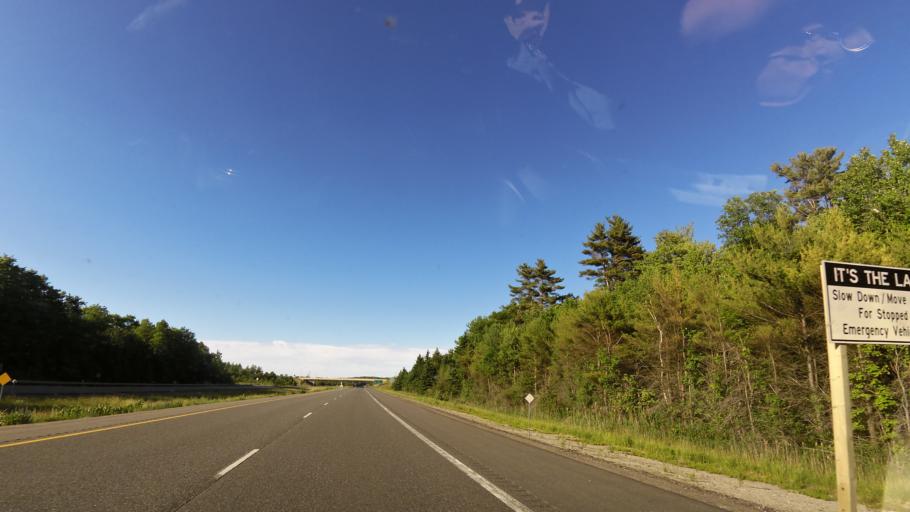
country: CA
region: Ontario
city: Barrie
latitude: 44.5487
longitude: -79.7488
